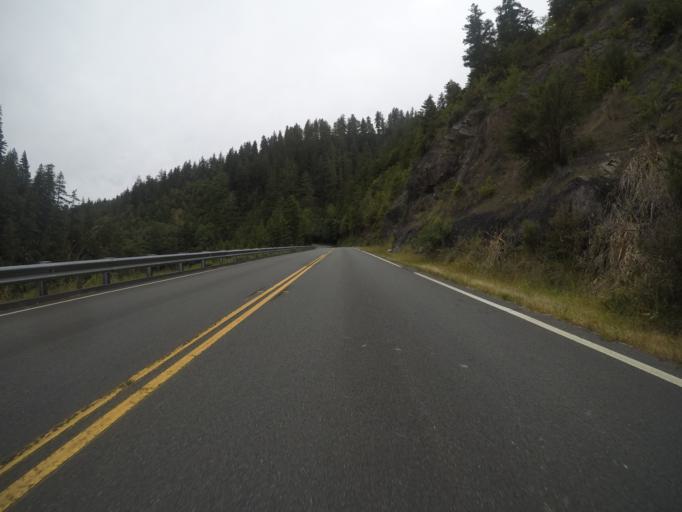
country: US
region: California
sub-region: Del Norte County
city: Bertsch-Oceanview
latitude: 41.7747
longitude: -124.0151
